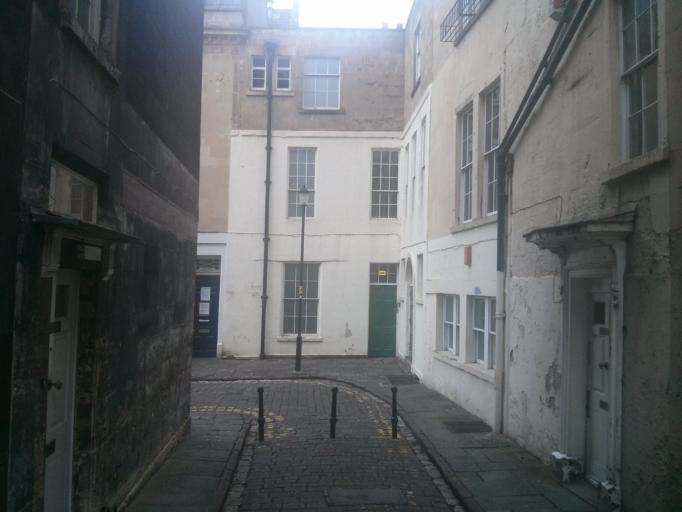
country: GB
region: England
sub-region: Bath and North East Somerset
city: Bath
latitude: 51.3826
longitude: -2.3614
